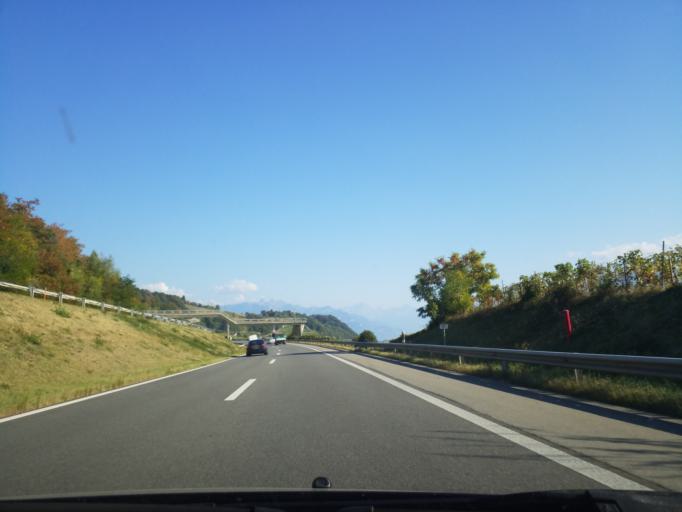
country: CH
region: Vaud
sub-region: Lavaux-Oron District
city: Cully
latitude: 46.4982
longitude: 6.7390
